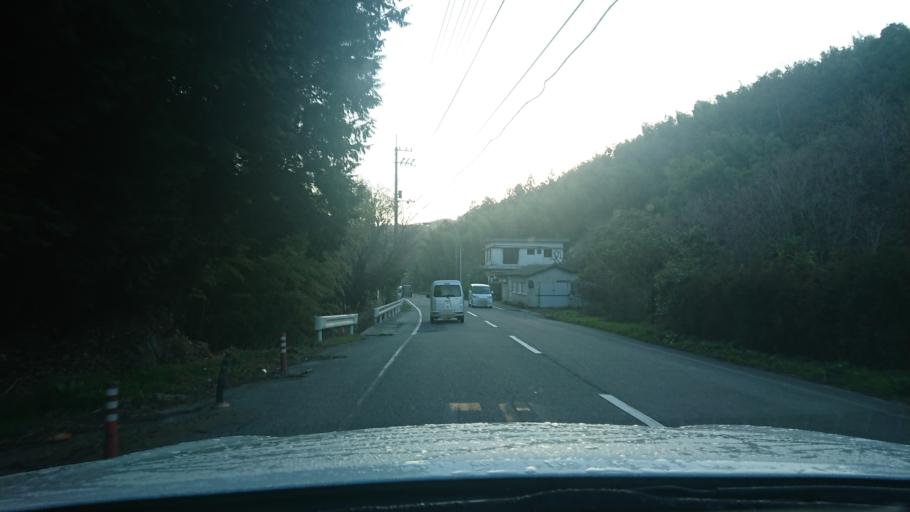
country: JP
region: Tokushima
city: Komatsushimacho
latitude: 33.9478
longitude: 134.5703
